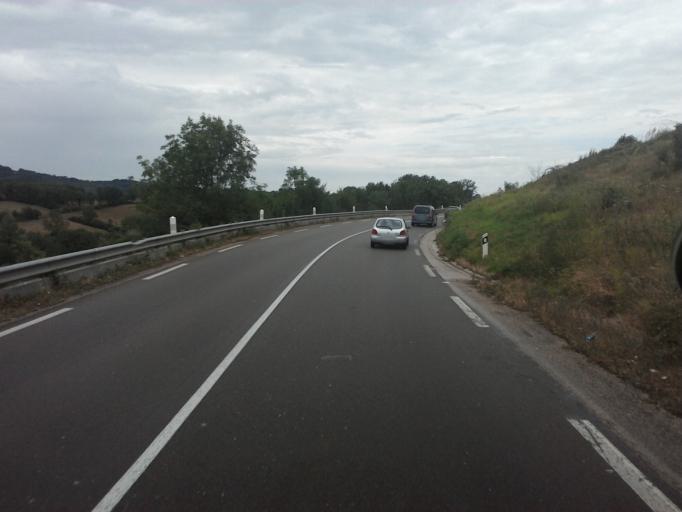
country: FR
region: Franche-Comte
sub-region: Departement du Jura
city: Poligny
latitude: 46.8798
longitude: 5.7184
